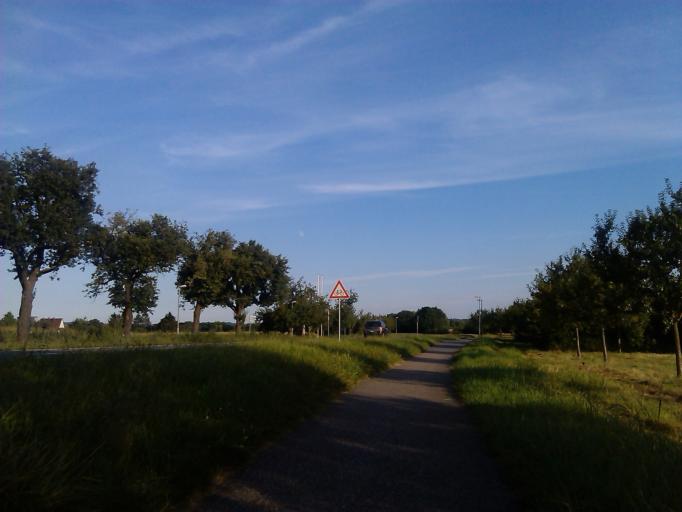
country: DE
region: Baden-Wuerttemberg
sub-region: Karlsruhe Region
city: Walldorf
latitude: 49.2968
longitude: 8.6520
